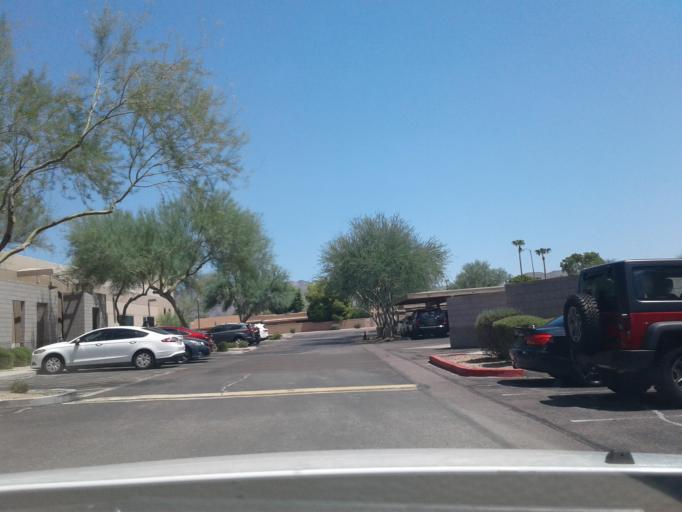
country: US
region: Arizona
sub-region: Maricopa County
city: Paradise Valley
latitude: 33.6175
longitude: -111.8880
